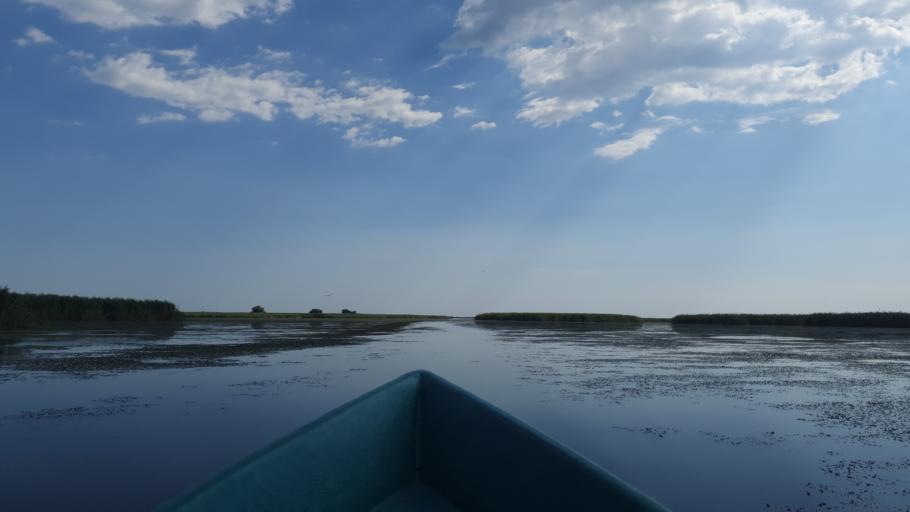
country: RU
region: Astrakhan
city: Kirovskiy
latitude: 45.8410
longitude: 48.4423
